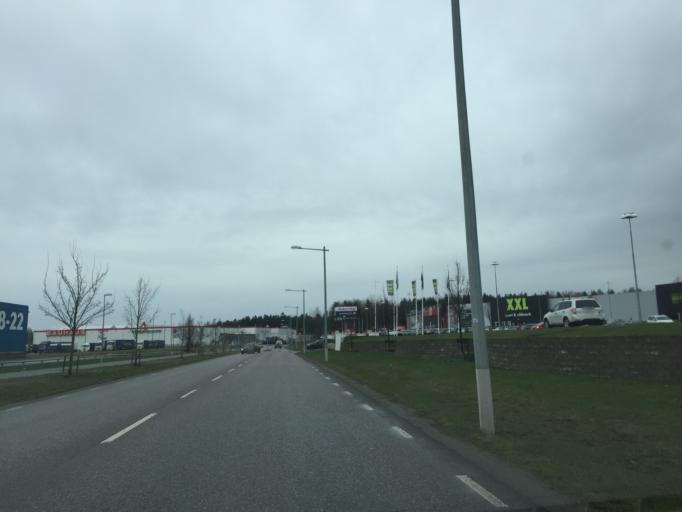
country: SE
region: OErebro
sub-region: Orebro Kommun
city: Orebro
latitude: 59.2177
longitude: 15.1410
